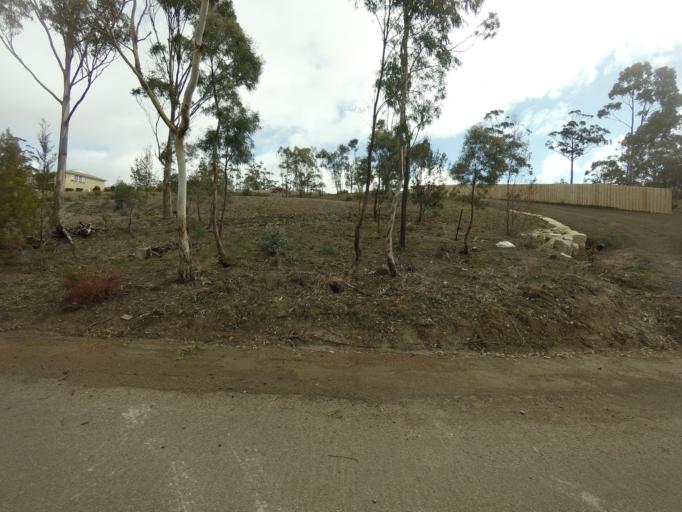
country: AU
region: Tasmania
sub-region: Sorell
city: Sorell
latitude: -42.5381
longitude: 147.9135
